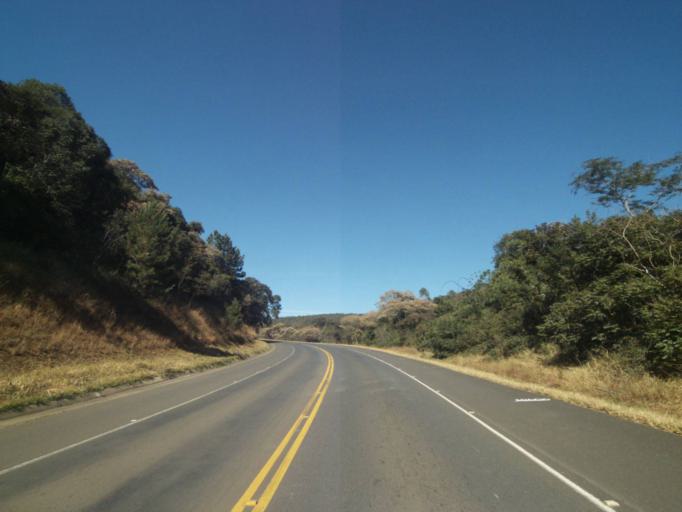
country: BR
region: Parana
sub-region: Tibagi
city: Tibagi
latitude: -24.5536
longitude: -50.4566
